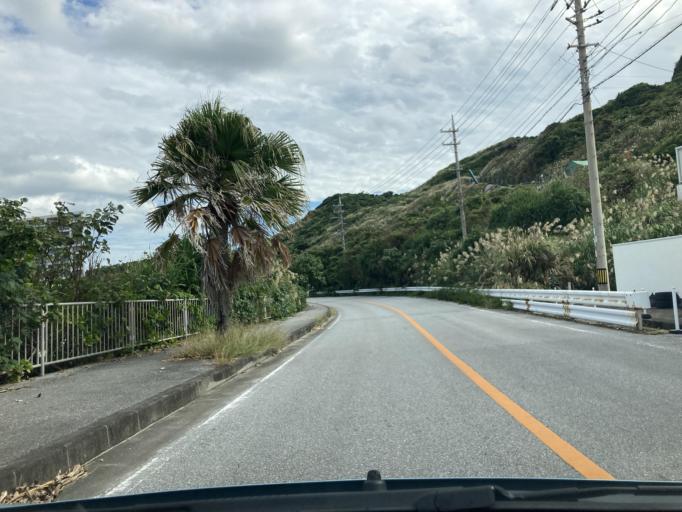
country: JP
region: Okinawa
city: Ishikawa
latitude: 26.4348
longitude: 127.7852
